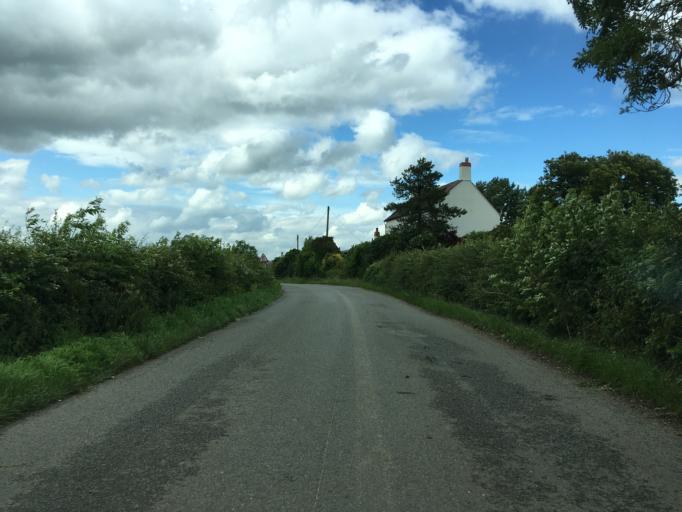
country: GB
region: England
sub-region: Gloucestershire
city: Stonehouse
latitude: 51.8049
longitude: -2.3433
